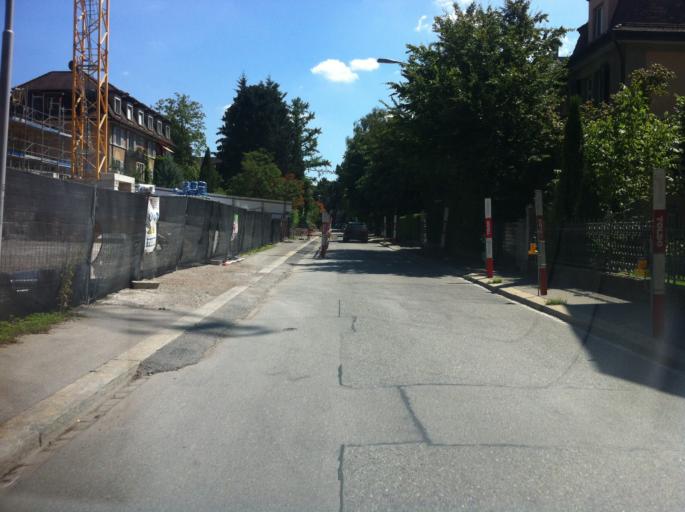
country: CH
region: Zurich
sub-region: Bezirk Zuerich
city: Zuerich (Kreis 8)
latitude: 47.3522
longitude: 8.5628
